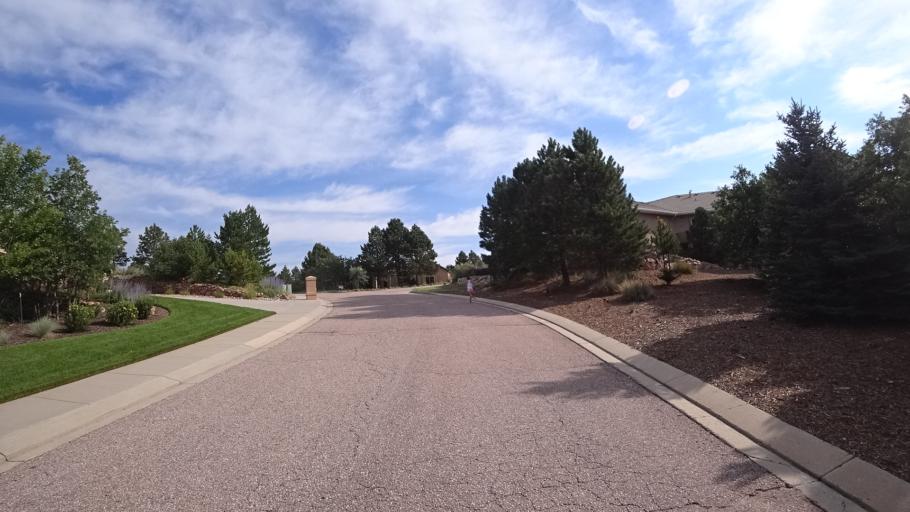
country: US
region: Colorado
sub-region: El Paso County
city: Air Force Academy
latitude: 38.9419
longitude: -104.8295
